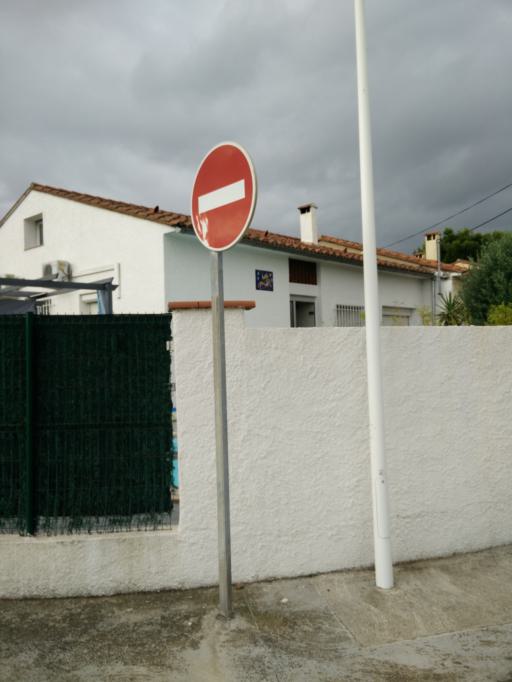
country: FR
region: Languedoc-Roussillon
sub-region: Departement des Pyrenees-Orientales
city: Saleilles
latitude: 42.6547
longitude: 2.9473
